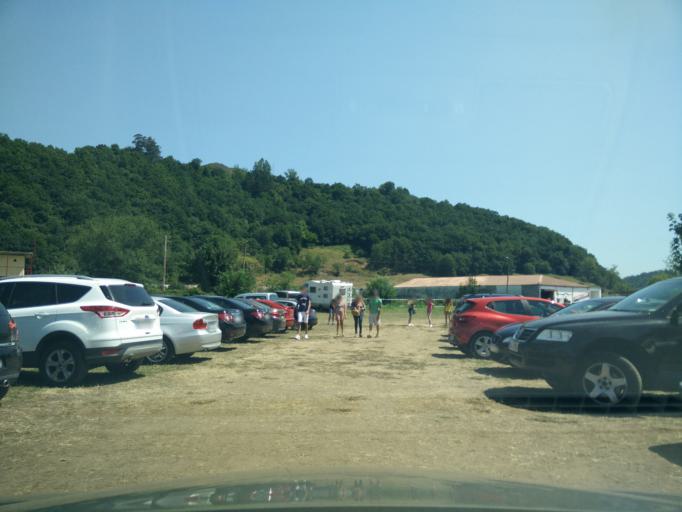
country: ES
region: Asturias
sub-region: Province of Asturias
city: Cangas de Onis
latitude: 43.3538
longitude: -5.1299
